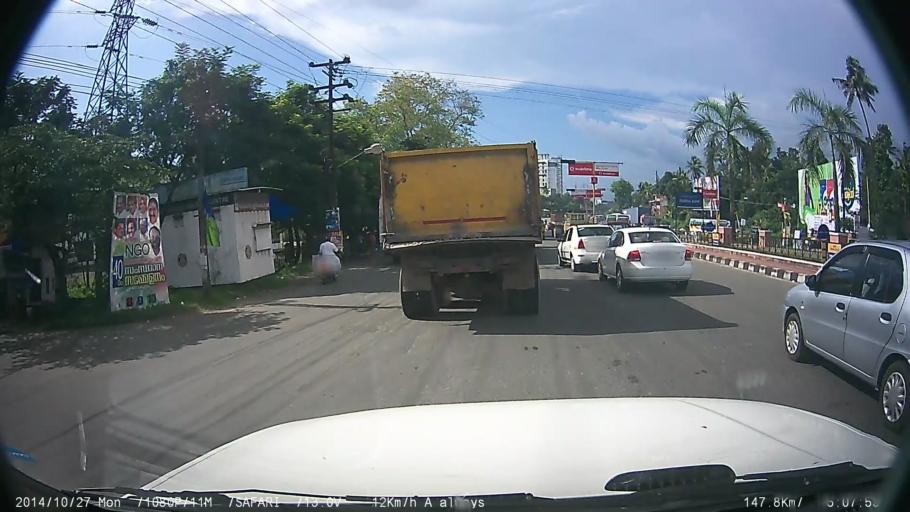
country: IN
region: Kerala
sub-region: Ernakulam
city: Aluva
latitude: 10.1133
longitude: 76.3467
